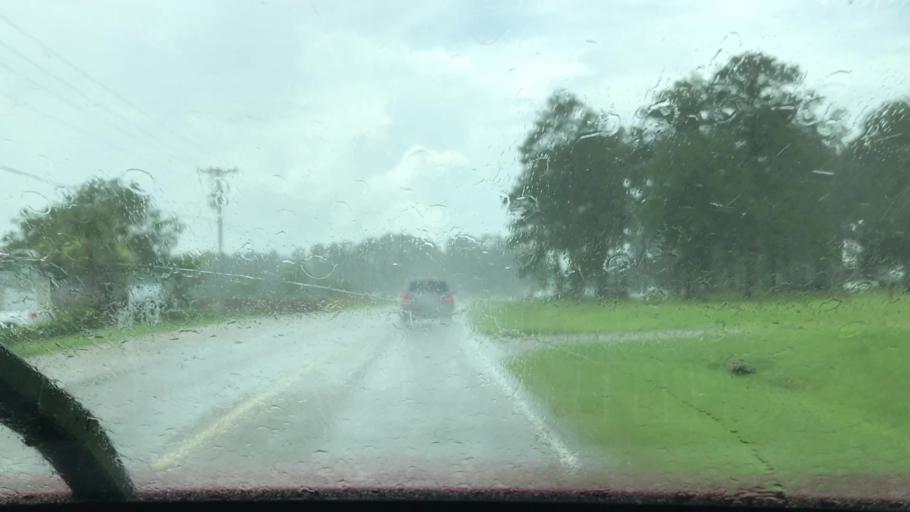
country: US
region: South Carolina
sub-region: Horry County
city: Red Hill
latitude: 33.8645
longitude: -78.9894
